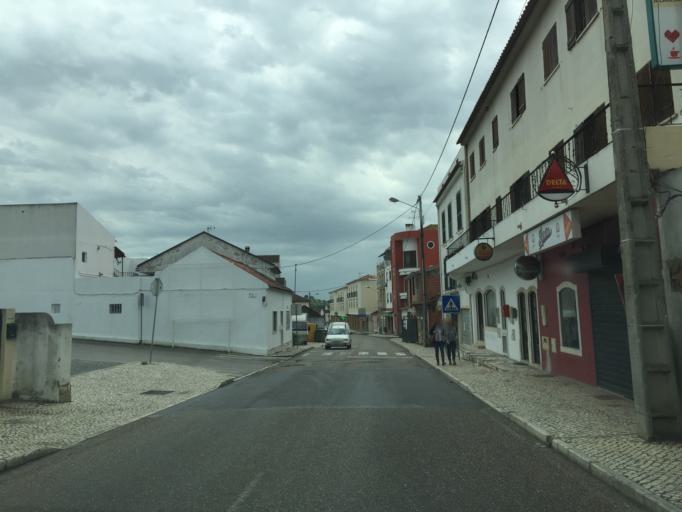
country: PT
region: Lisbon
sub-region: Azambuja
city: Aveiras de Cima
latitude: 39.1396
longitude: -8.8996
